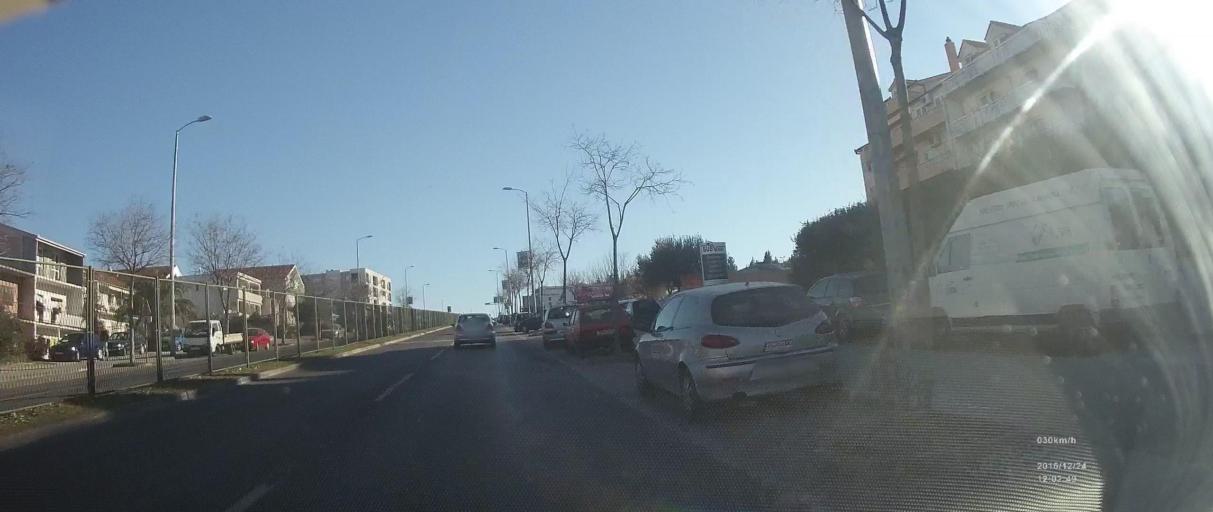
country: HR
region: Splitsko-Dalmatinska
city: Kamen
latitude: 43.5157
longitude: 16.4900
